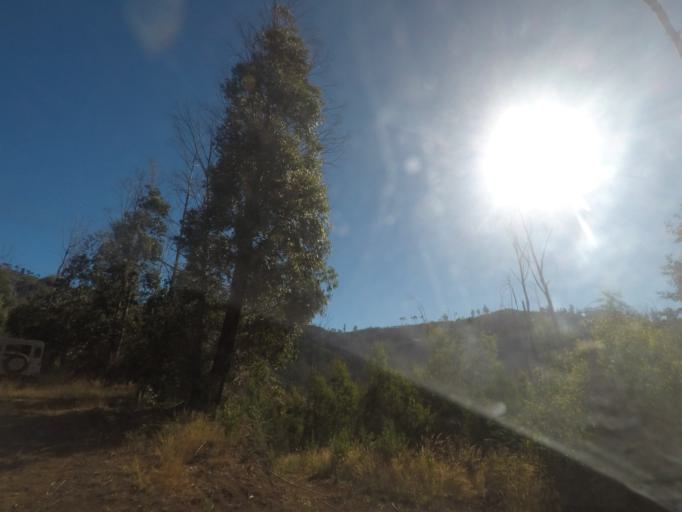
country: PT
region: Madeira
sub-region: Funchal
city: Nossa Senhora do Monte
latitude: 32.6921
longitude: -16.9130
